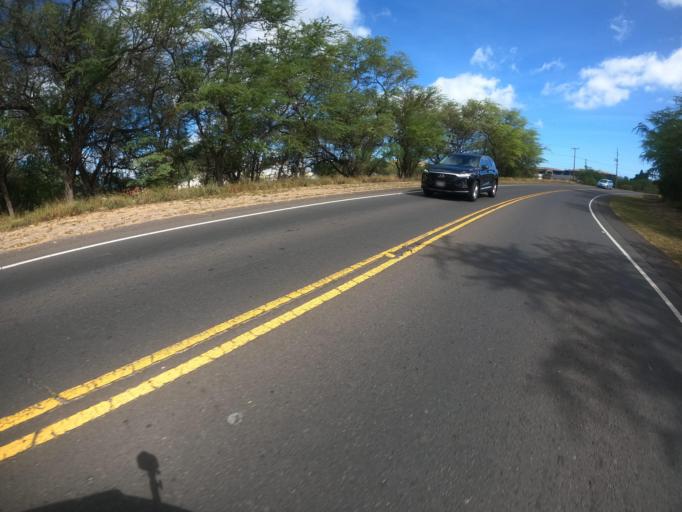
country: US
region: Hawaii
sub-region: Honolulu County
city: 'Ewa Villages
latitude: 21.3311
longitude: -158.0412
